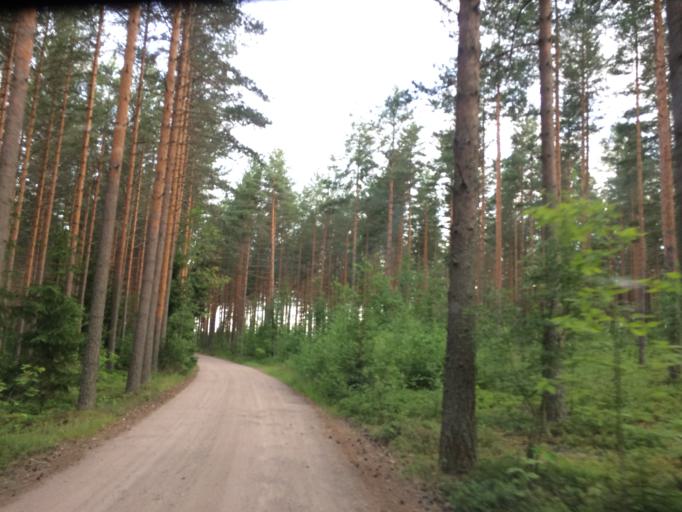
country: FI
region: Haeme
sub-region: Haemeenlinna
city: Janakkala
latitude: 60.8928
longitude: 24.6061
